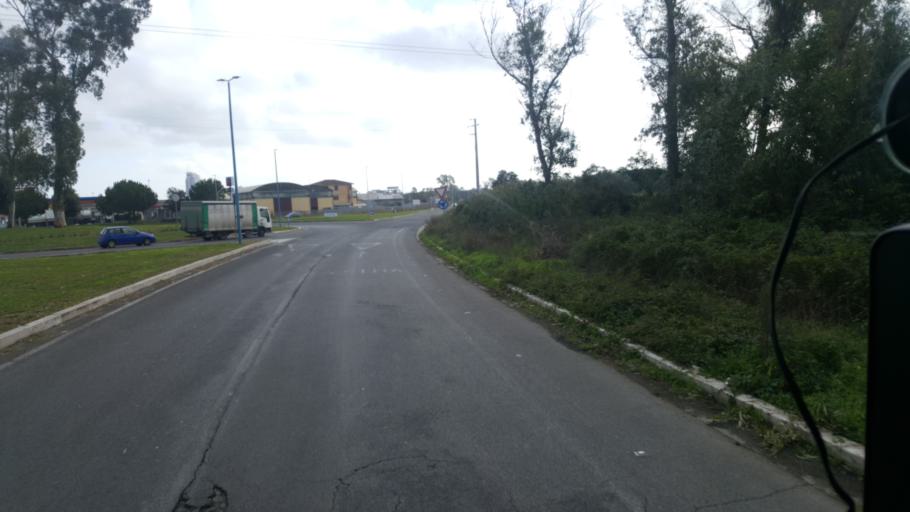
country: IT
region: Latium
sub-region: Provincia di Latina
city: Latina
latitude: 41.4780
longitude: 12.8736
